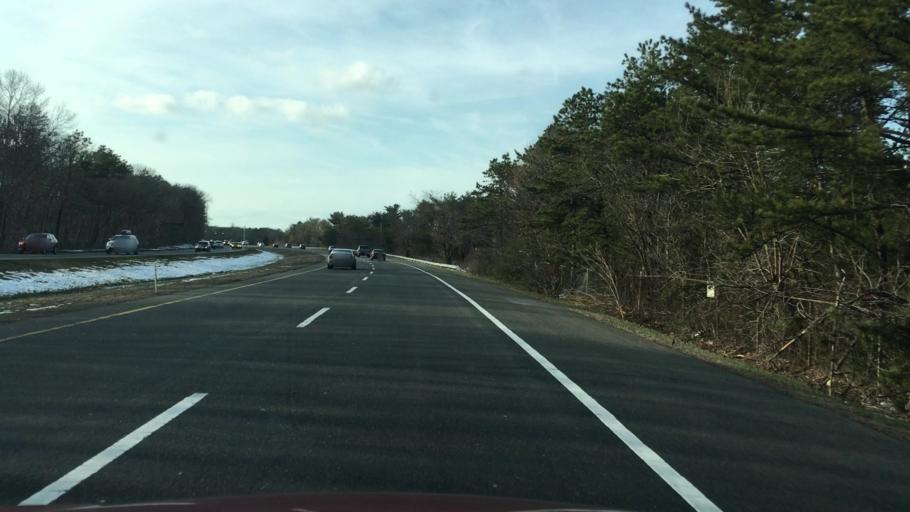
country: US
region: New York
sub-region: Suffolk County
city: Centereach
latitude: 40.8744
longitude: -73.0707
